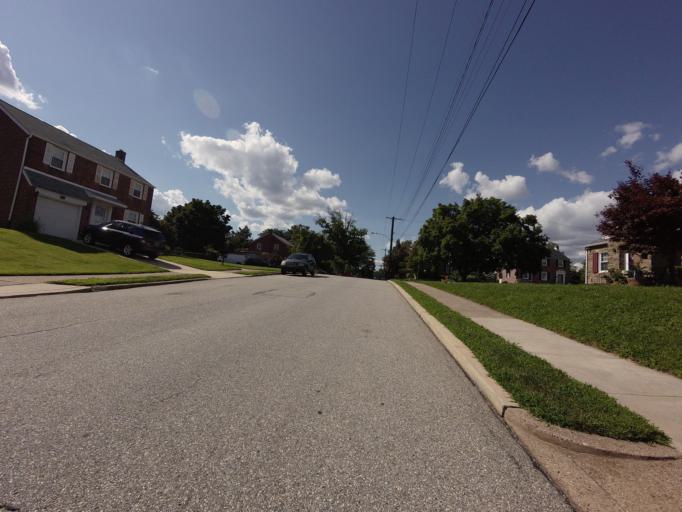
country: US
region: Pennsylvania
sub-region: Montgomery County
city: Bala-Cynwyd
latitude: 40.0262
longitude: -75.2060
